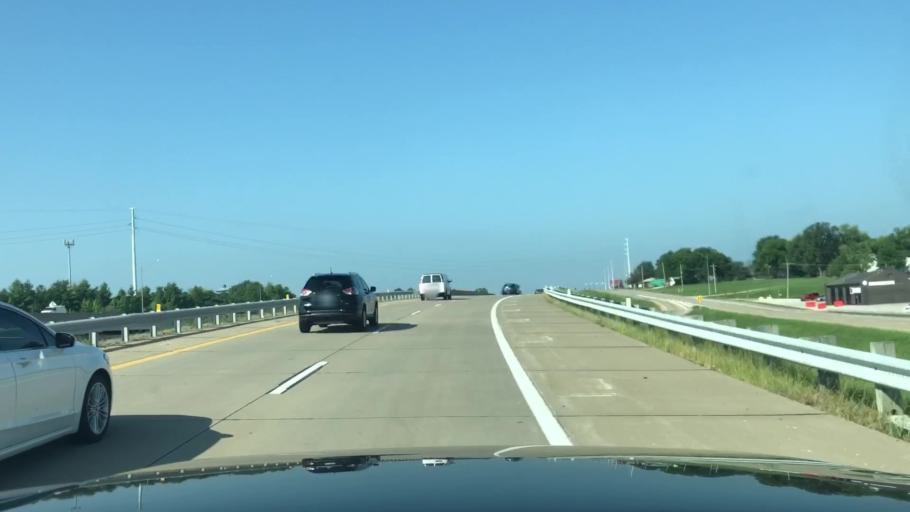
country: US
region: Missouri
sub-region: Saint Charles County
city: Saint Charles
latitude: 38.7552
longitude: -90.5468
